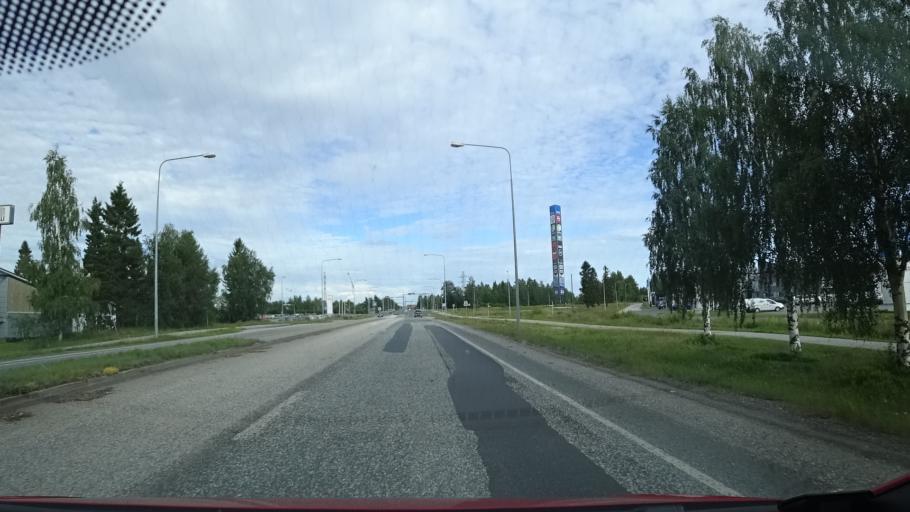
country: FI
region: Lapland
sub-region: Kemi-Tornio
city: Keminmaa
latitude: 65.7986
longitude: 24.5099
